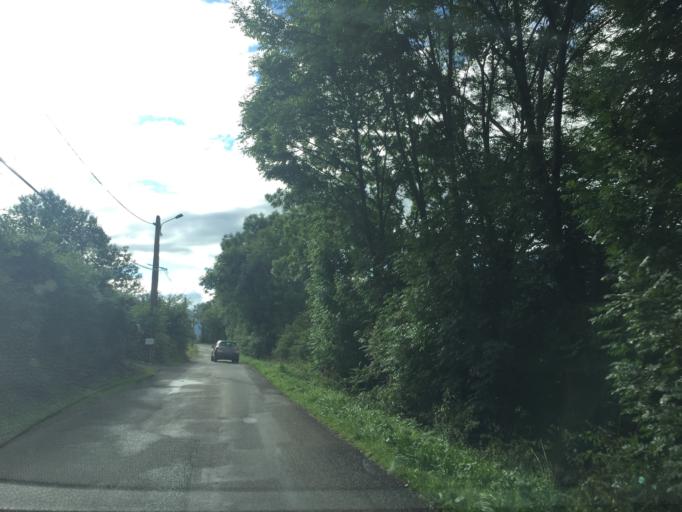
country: FR
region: Midi-Pyrenees
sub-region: Departement de la Haute-Garonne
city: Bagneres-de-Luchon
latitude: 42.8108
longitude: 0.4980
